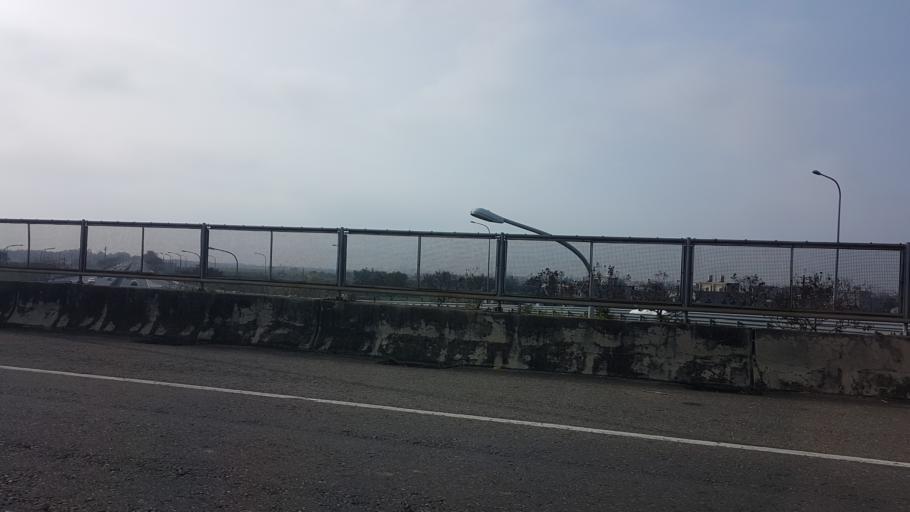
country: TW
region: Taiwan
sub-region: Chiayi
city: Taibao
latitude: 23.4288
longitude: 120.3182
